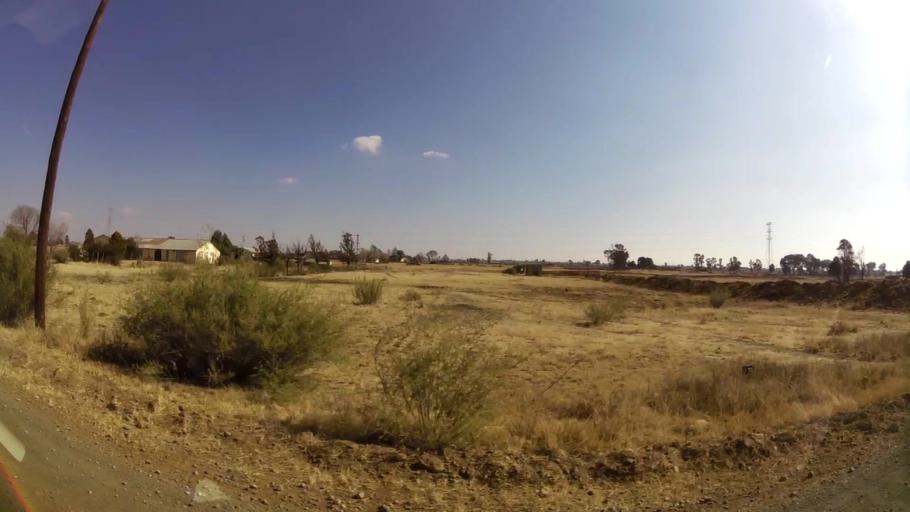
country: ZA
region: Orange Free State
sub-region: Mangaung Metropolitan Municipality
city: Bloemfontein
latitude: -29.1705
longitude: 26.3082
